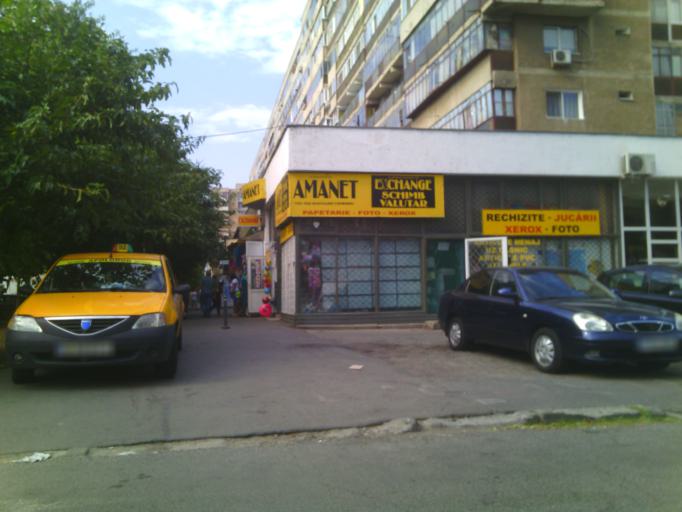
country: RO
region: Bucuresti
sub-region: Municipiul Bucuresti
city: Bucuresti
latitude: 44.3835
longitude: 26.0925
